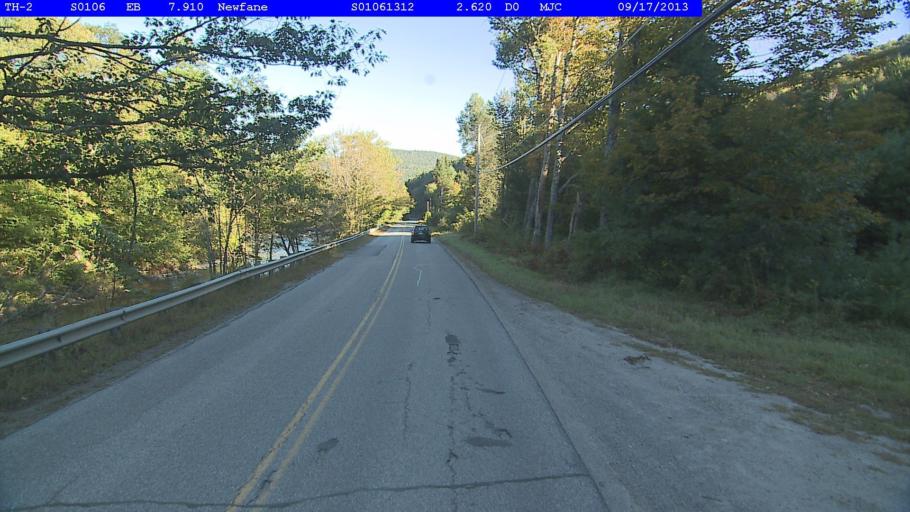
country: US
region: Vermont
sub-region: Windham County
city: Newfane
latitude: 42.9401
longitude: -72.7223
